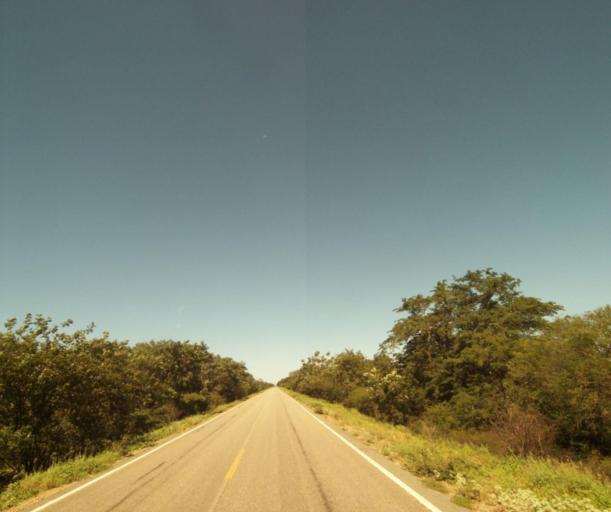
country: BR
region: Bahia
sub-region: Palmas De Monte Alto
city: Palmas de Monte Alto
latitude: -14.2618
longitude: -43.3131
